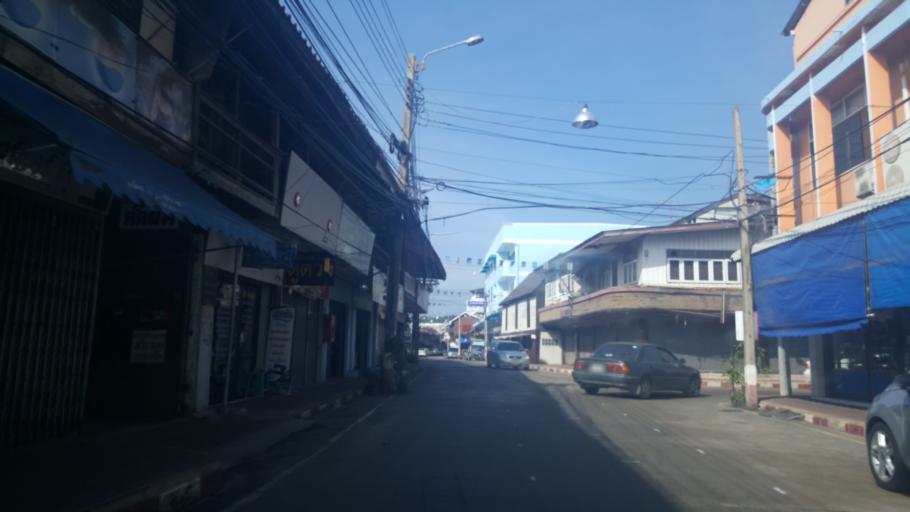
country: TH
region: Chon Buri
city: Sattahip
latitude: 12.6629
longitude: 100.9017
